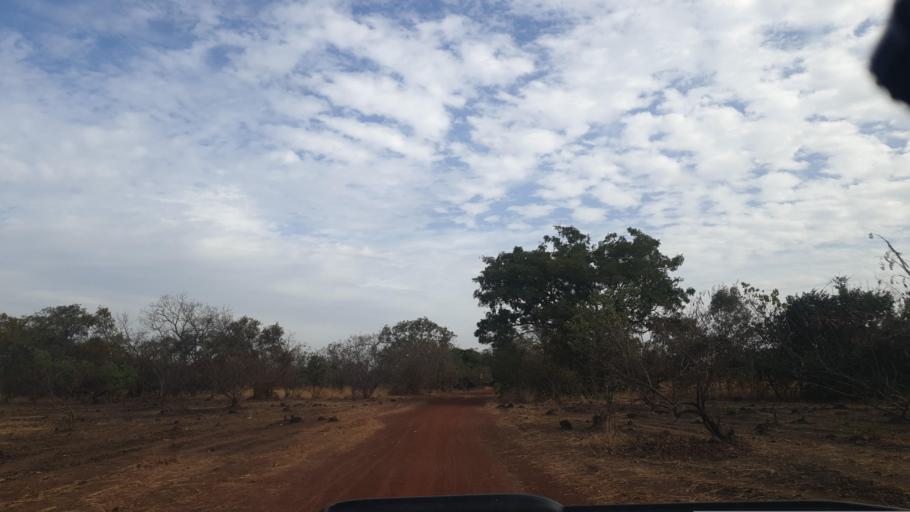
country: ML
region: Sikasso
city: Yanfolila
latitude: 11.3976
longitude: -8.0182
